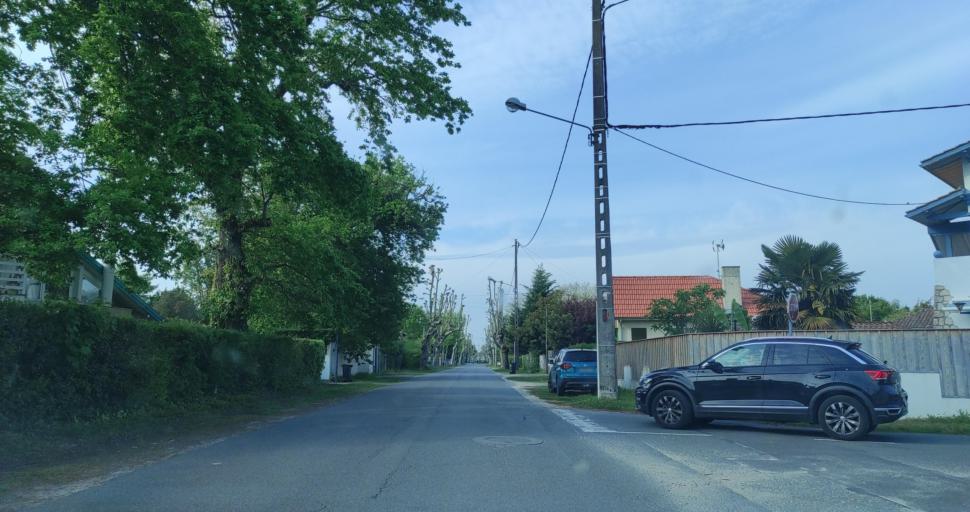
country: FR
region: Aquitaine
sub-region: Departement de la Gironde
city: Ares
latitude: 44.7584
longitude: -1.1330
